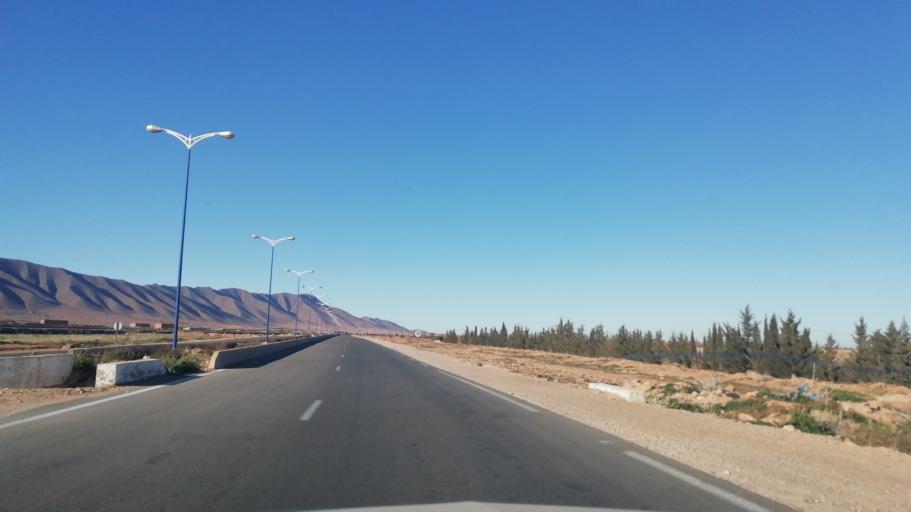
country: DZ
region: Wilaya de Naama
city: Naama
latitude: 33.5614
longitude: -0.2375
